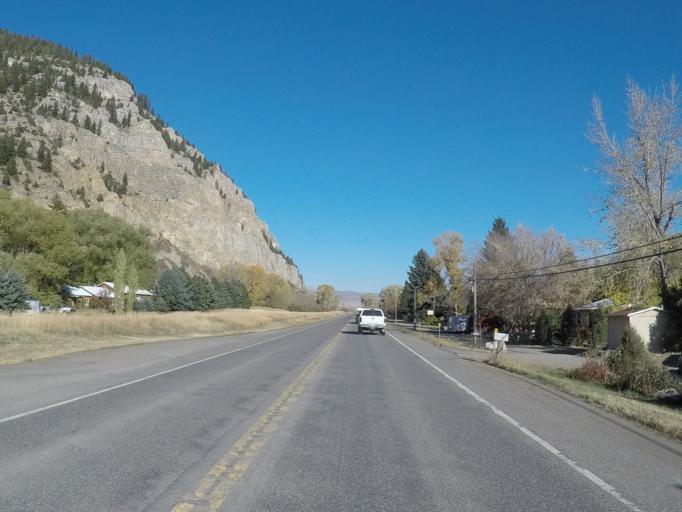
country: US
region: Montana
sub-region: Park County
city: Livingston
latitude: 45.6060
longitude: -110.5751
